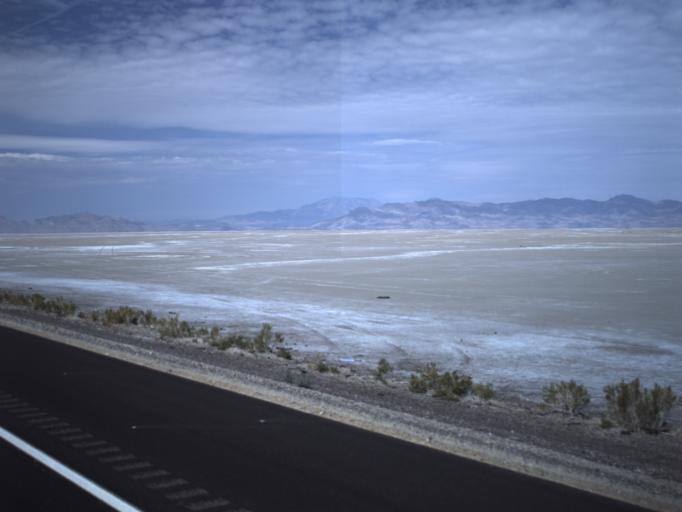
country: US
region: Utah
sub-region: Tooele County
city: Wendover
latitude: 40.7339
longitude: -113.5935
